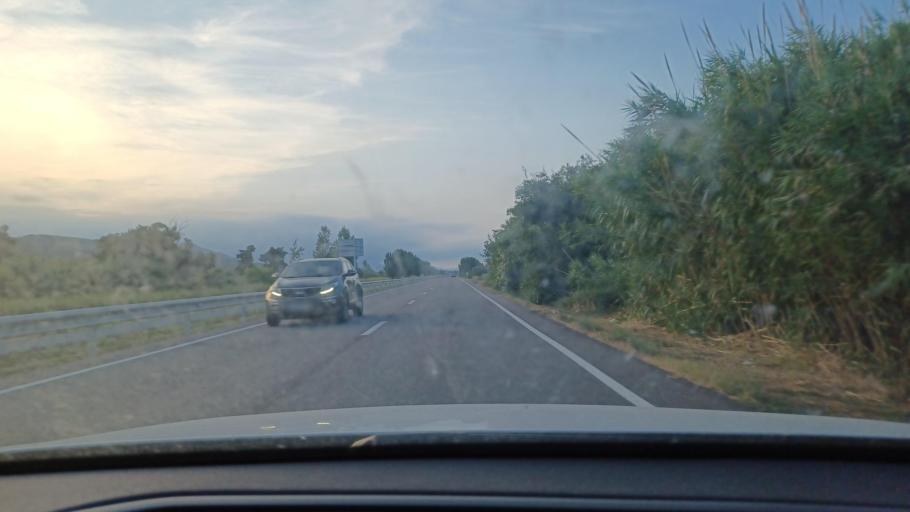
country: ES
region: Catalonia
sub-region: Provincia de Tarragona
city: Sant Carles de la Rapita
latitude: 40.6459
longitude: 0.5990
